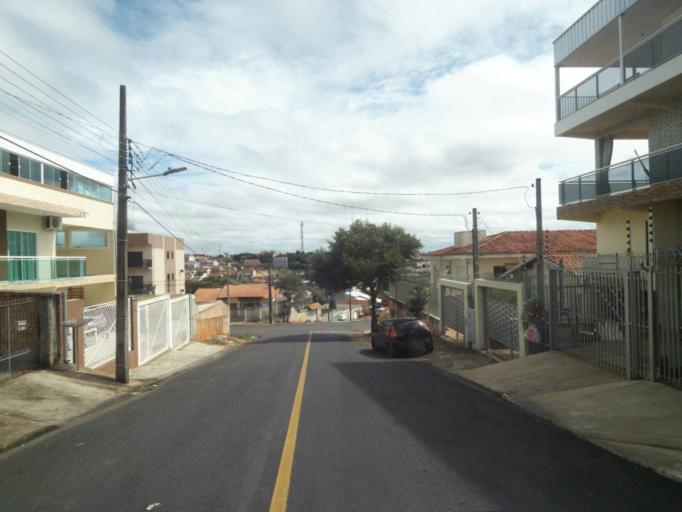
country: BR
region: Parana
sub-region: Telemaco Borba
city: Telemaco Borba
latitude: -24.3345
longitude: -50.6430
